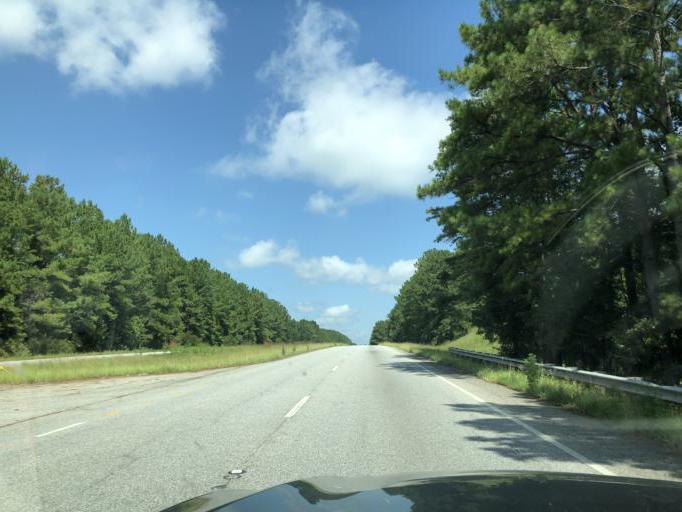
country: US
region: Alabama
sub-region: Henry County
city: Abbeville
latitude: 31.6759
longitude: -85.2793
